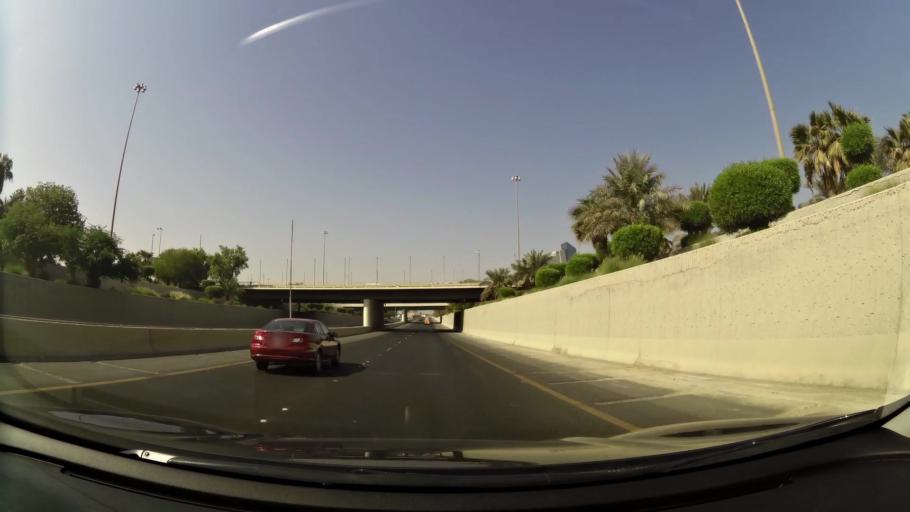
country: KW
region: Al Asimah
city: Kuwait City
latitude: 29.3590
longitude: 47.9754
